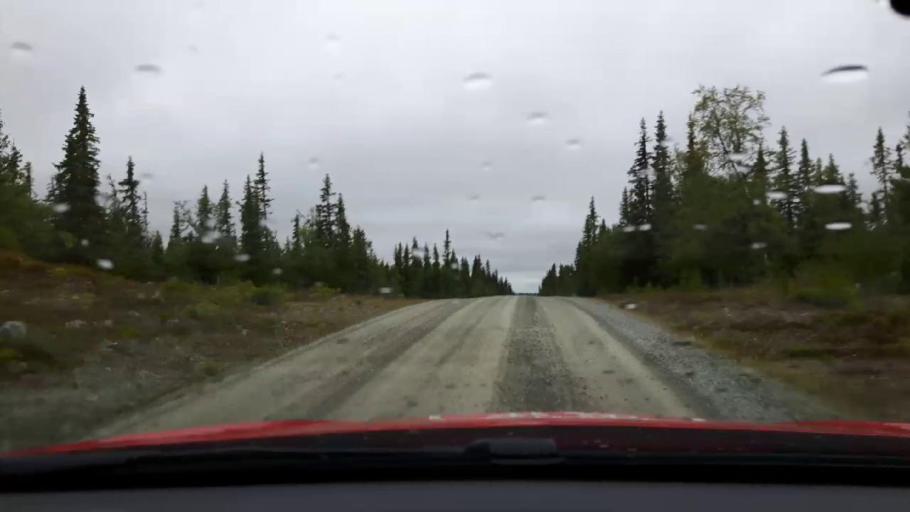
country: SE
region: Jaemtland
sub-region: Bergs Kommun
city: Hoverberg
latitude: 62.8568
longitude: 13.9321
